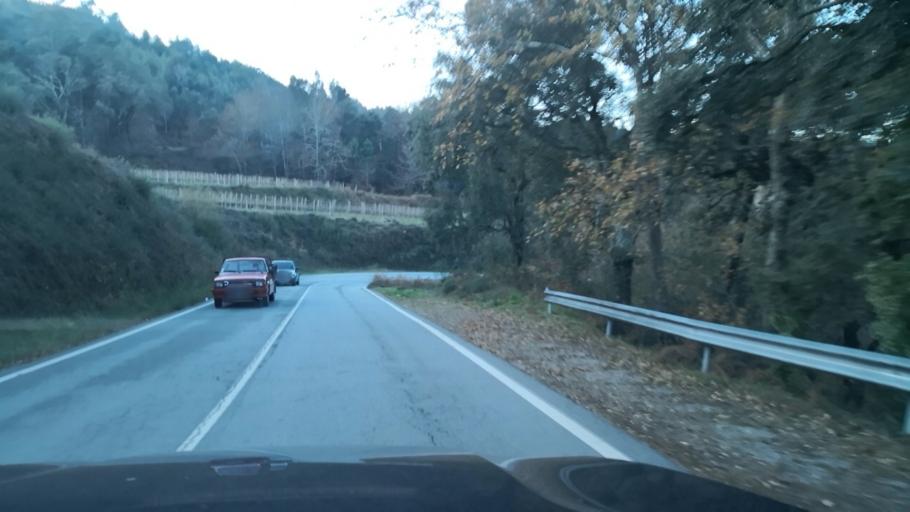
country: PT
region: Vila Real
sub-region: Mondim de Basto
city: Mondim de Basto
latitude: 41.4684
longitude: -7.9535
